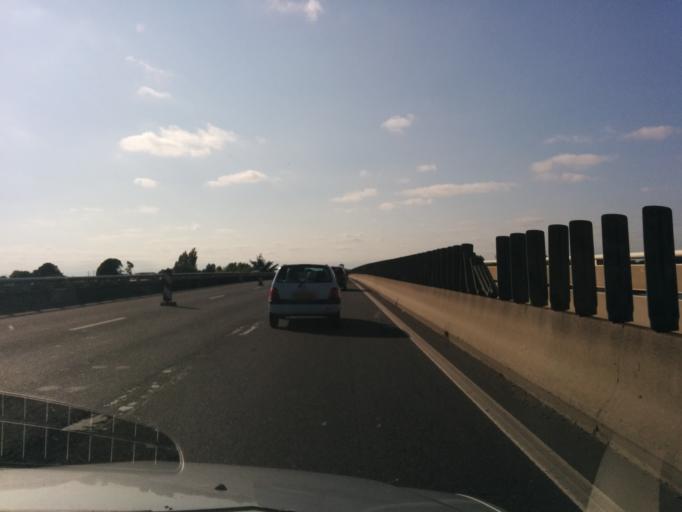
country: FR
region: Pays de la Loire
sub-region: Departement de la Loire-Atlantique
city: Basse-Goulaine
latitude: 47.2316
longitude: -1.4716
